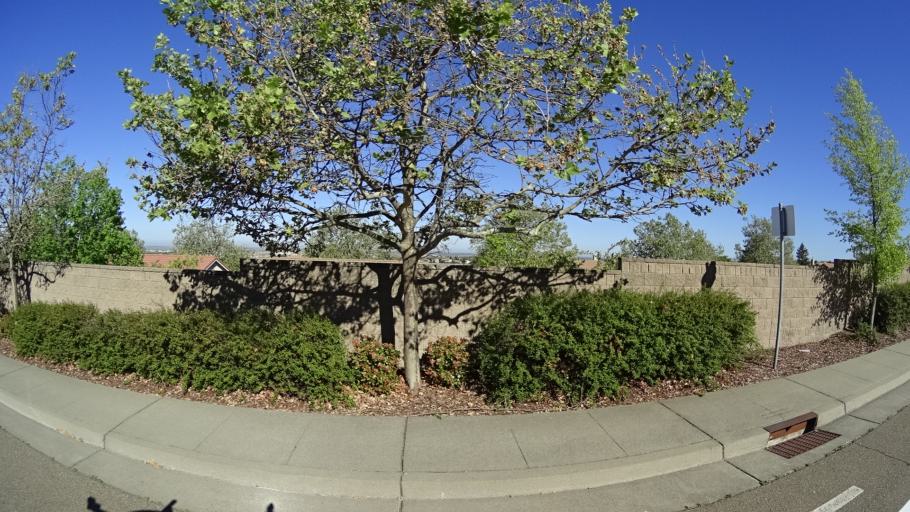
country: US
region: California
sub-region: Placer County
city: Rocklin
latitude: 38.8263
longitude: -121.2345
